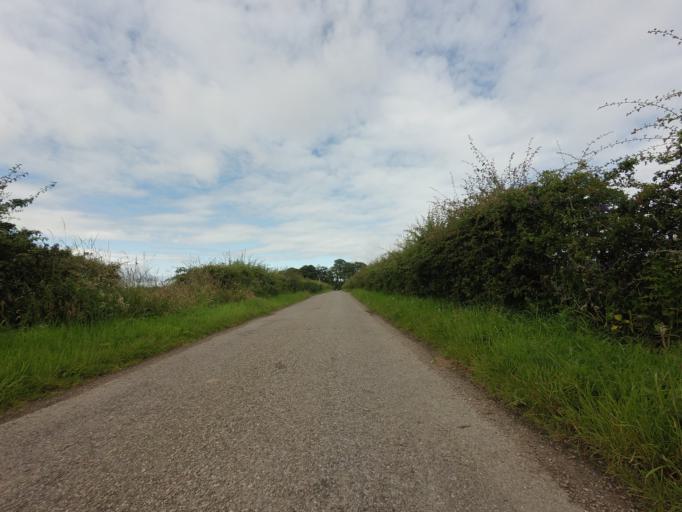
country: GB
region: Scotland
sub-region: Moray
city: Hopeman
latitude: 57.6702
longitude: -3.3939
